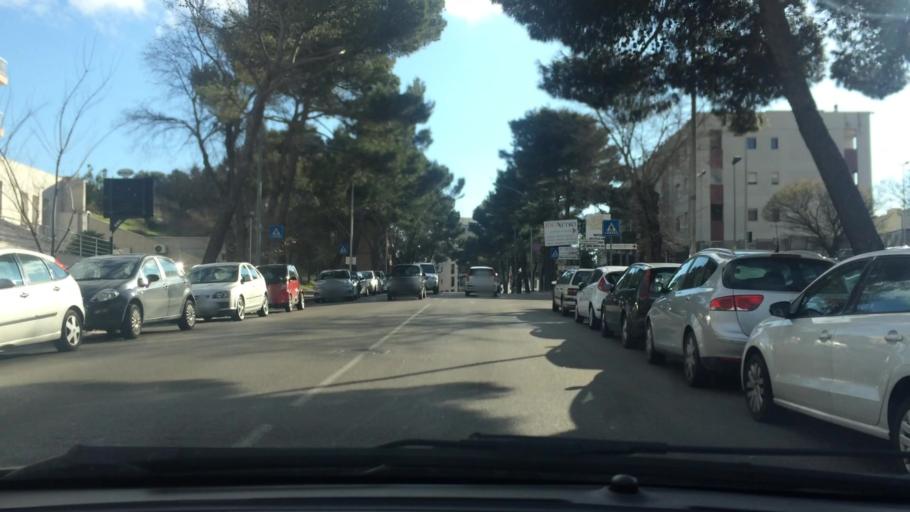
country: IT
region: Basilicate
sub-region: Provincia di Matera
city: Matera
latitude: 40.6701
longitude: 16.5976
